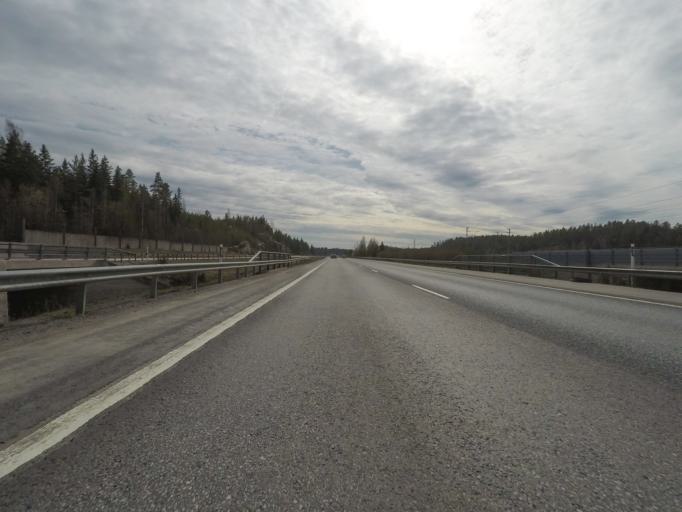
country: FI
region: Uusimaa
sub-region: Porvoo
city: Pukkila
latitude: 60.7329
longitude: 25.4461
